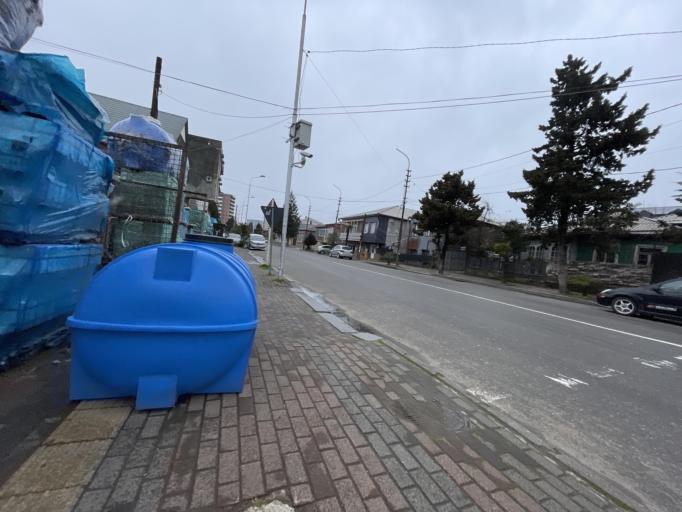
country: GE
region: Ajaria
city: Batumi
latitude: 41.6377
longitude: 41.6433
